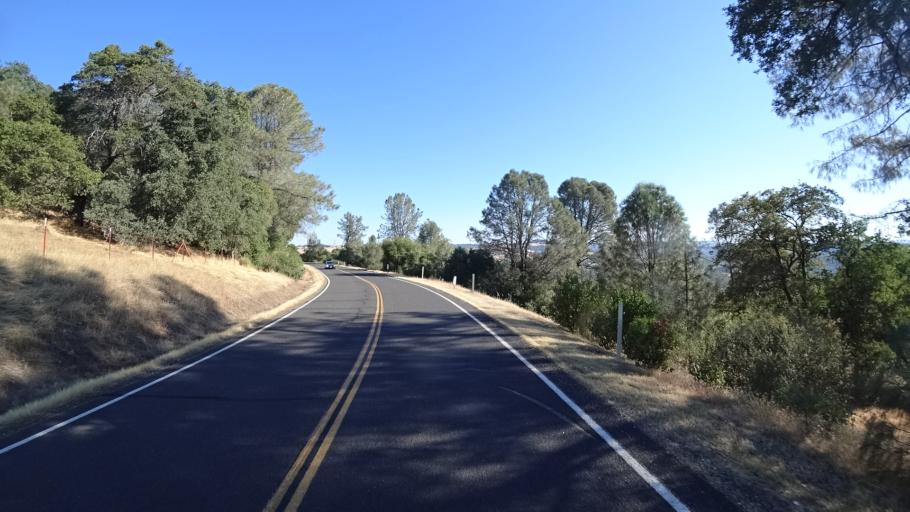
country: US
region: California
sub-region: Calaveras County
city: Angels Camp
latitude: 38.0817
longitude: -120.4819
